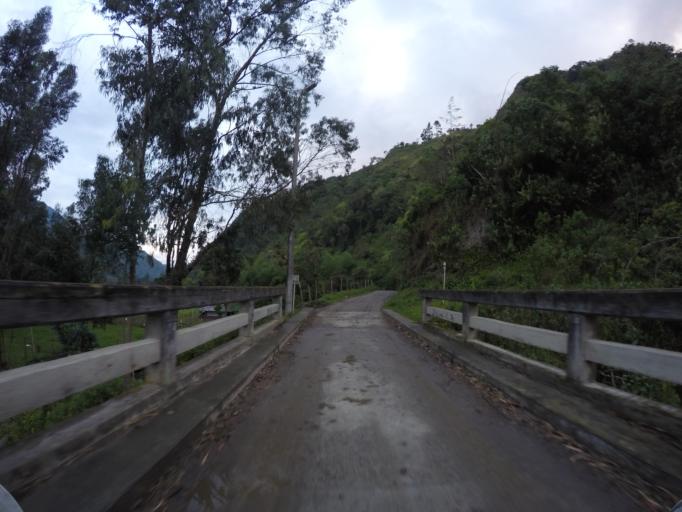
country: CO
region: Tolima
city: Cajamarca
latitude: 4.5179
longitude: -75.4093
